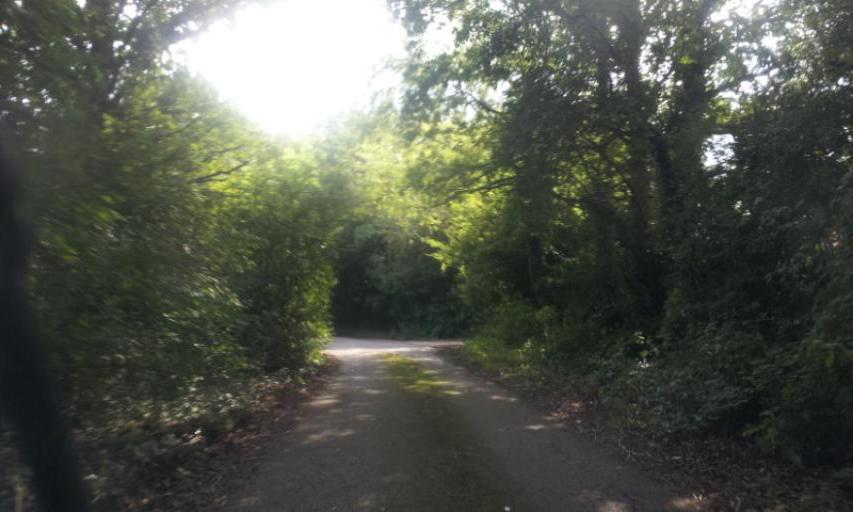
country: GB
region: England
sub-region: Kent
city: Hadlow
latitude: 51.2325
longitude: 0.3352
